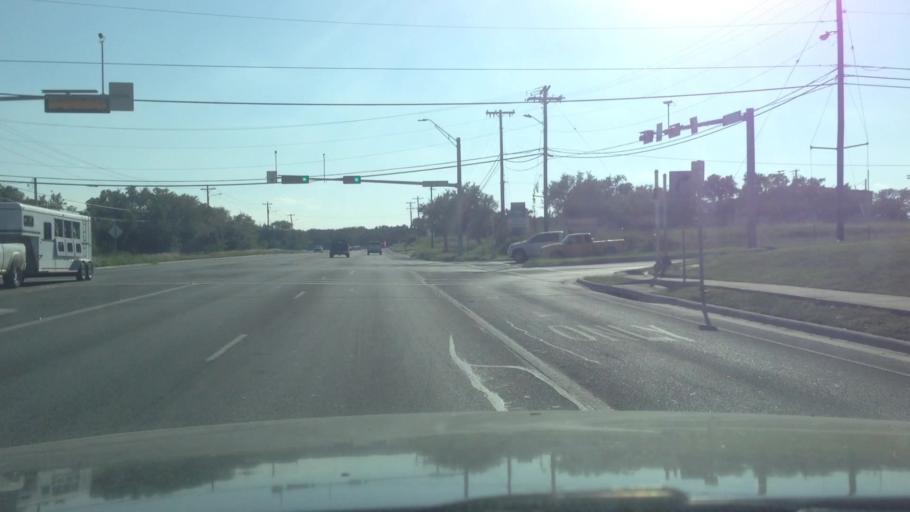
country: US
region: Texas
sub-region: Hays County
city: San Marcos
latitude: 29.8578
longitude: -97.9692
